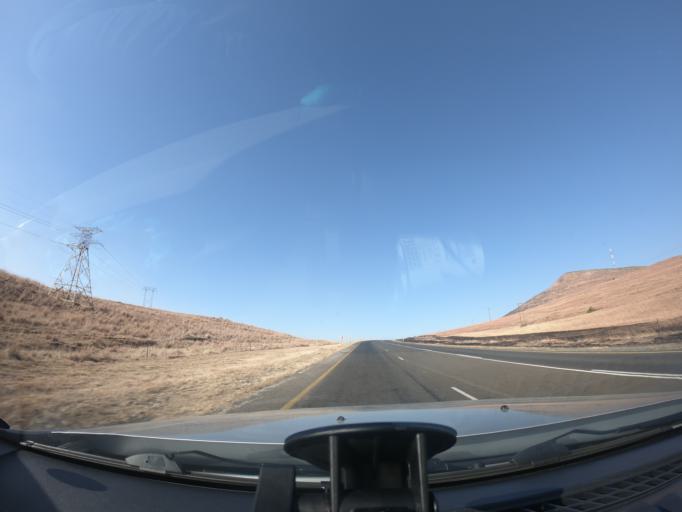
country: ZA
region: Mpumalanga
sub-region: Gert Sibande District Municipality
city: Volksrust
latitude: -27.2975
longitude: 29.8985
